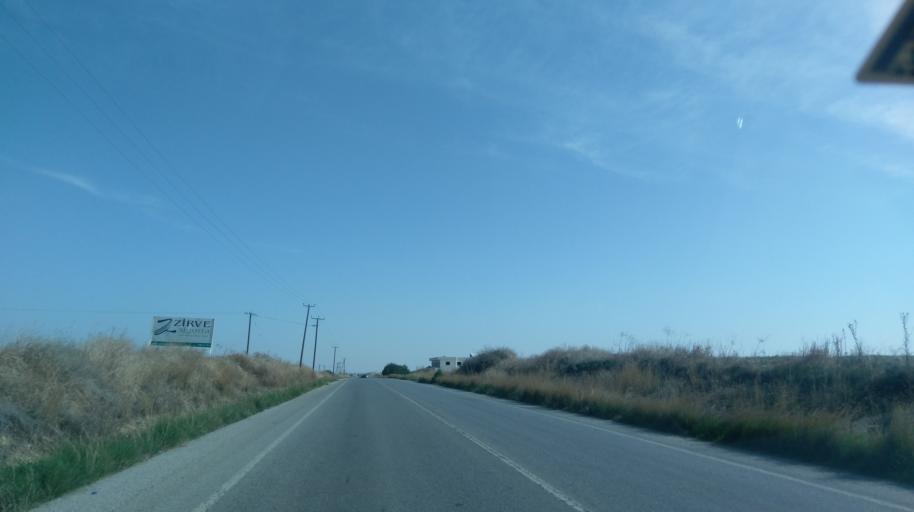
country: CY
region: Ammochostos
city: Lefkonoiko
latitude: 35.2355
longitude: 33.5739
